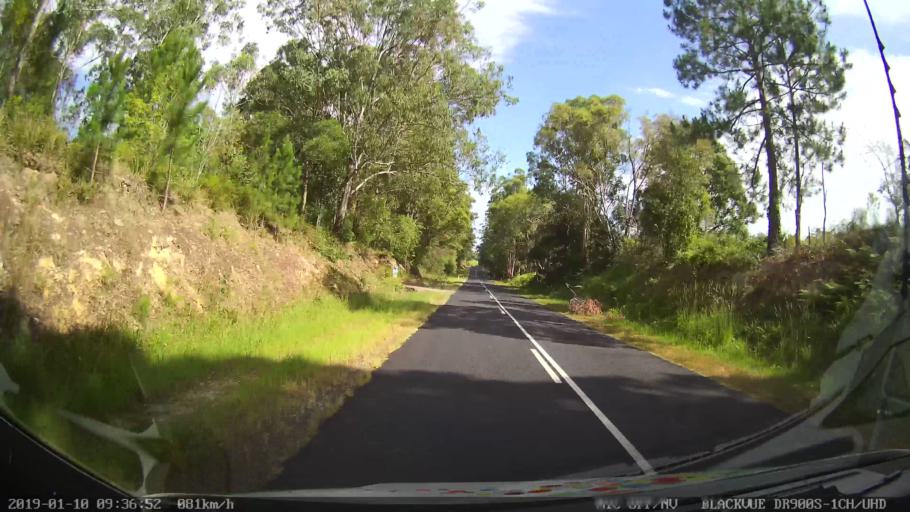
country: AU
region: New South Wales
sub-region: Coffs Harbour
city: Nana Glen
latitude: -30.1942
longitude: 153.0129
